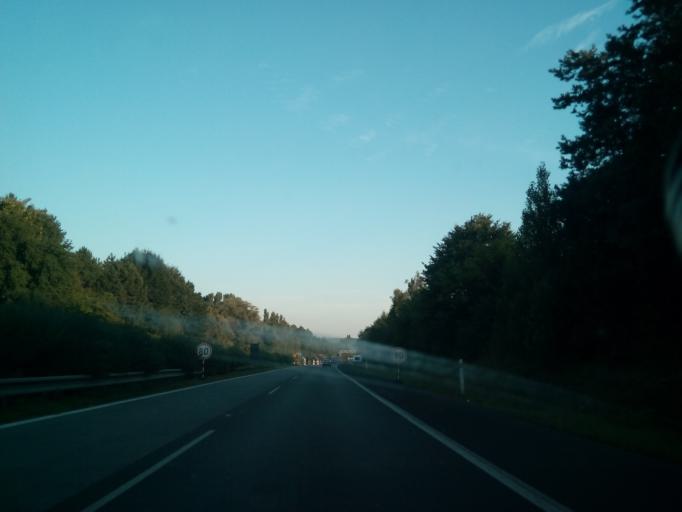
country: SK
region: Presovsky
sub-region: Okres Presov
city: Presov
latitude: 48.9473
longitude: 21.2561
